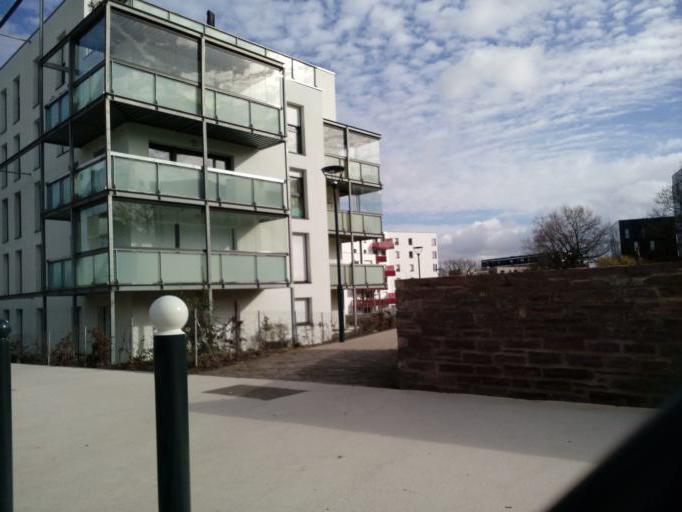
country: FR
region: Brittany
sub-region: Departement d'Ille-et-Vilaine
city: Saint-Gregoire
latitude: 48.1337
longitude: -1.6980
